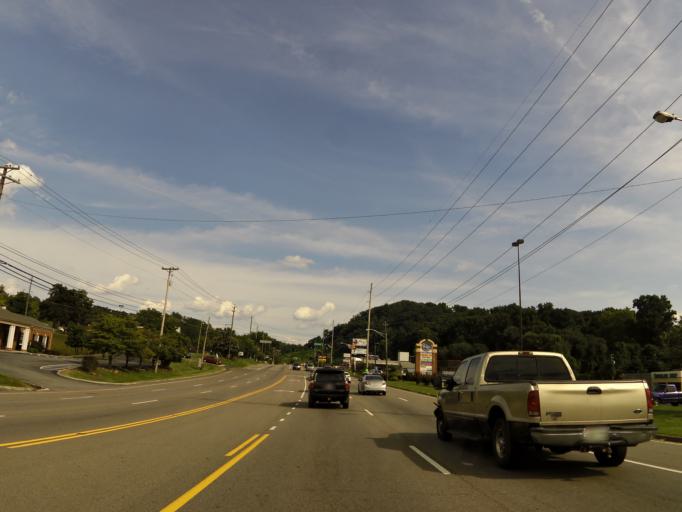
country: US
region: Tennessee
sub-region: Knox County
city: Knoxville
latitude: 35.9335
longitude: -83.9049
